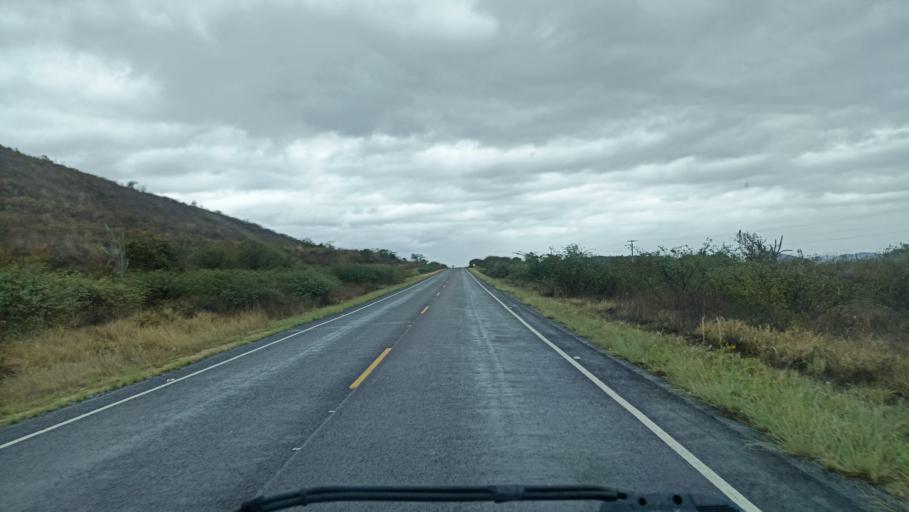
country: BR
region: Bahia
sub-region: Iacu
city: Iacu
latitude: -12.9582
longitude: -40.4725
